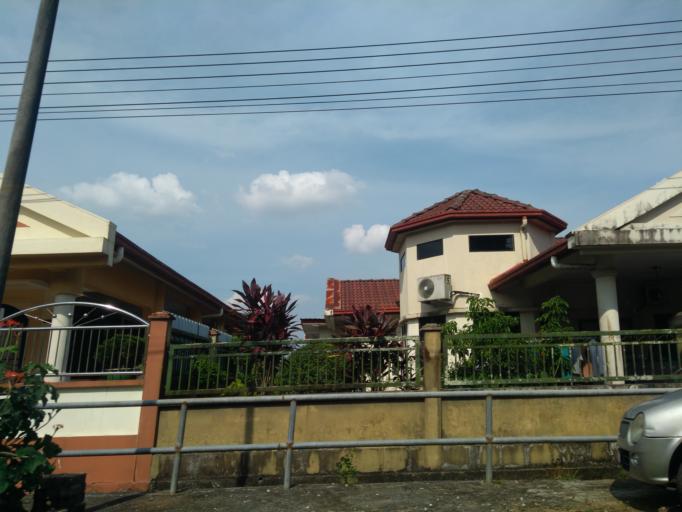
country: MY
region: Sarawak
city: Kuching
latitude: 1.5788
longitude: 110.2939
